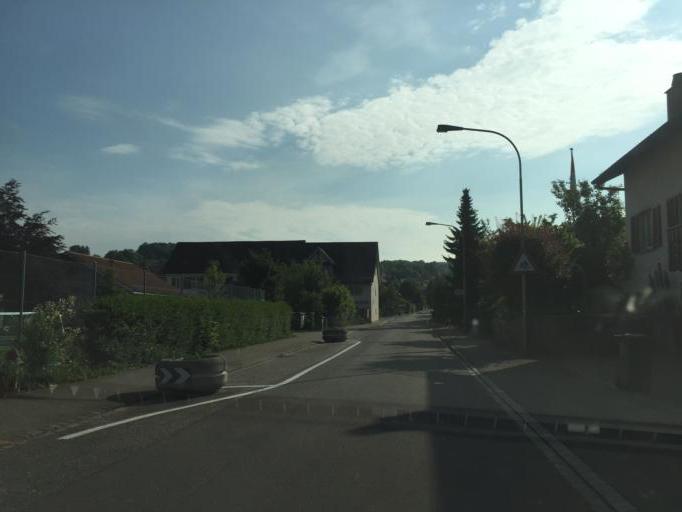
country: CH
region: Zurich
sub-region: Bezirk Buelach
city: Bachenbulach
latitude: 47.5018
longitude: 8.5461
